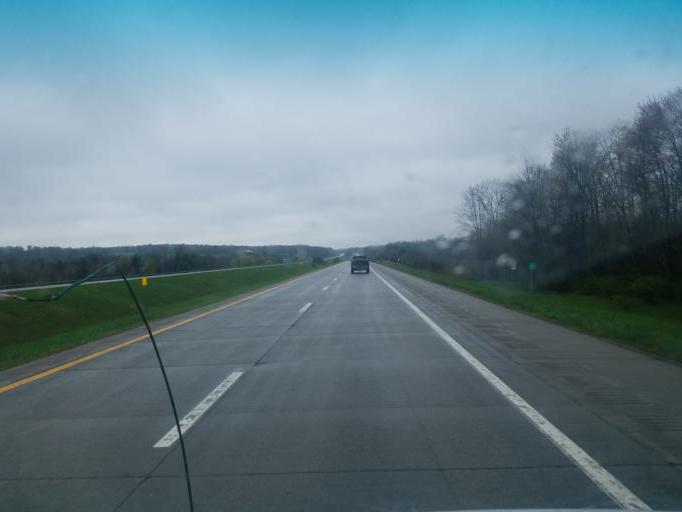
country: US
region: New York
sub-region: Chautauqua County
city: Mayville
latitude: 42.1569
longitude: -79.5558
